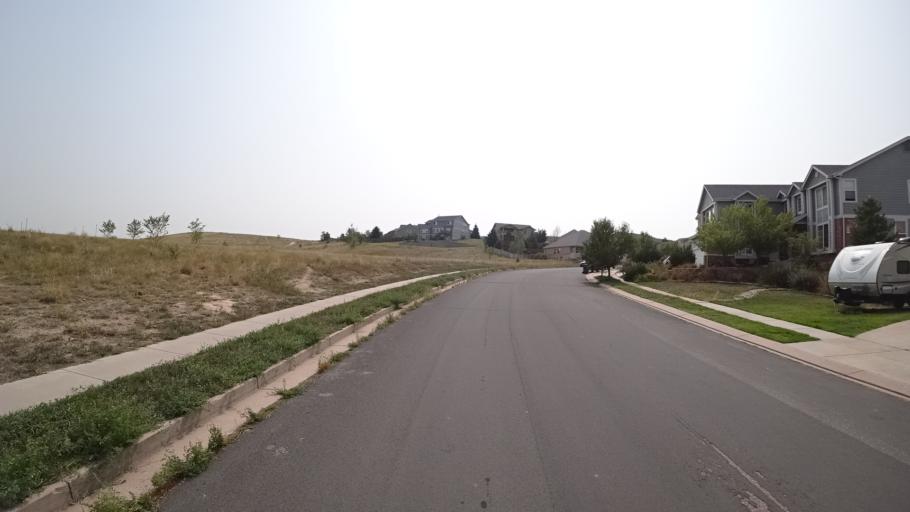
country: US
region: Colorado
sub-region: El Paso County
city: Cimarron Hills
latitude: 38.9265
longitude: -104.7449
